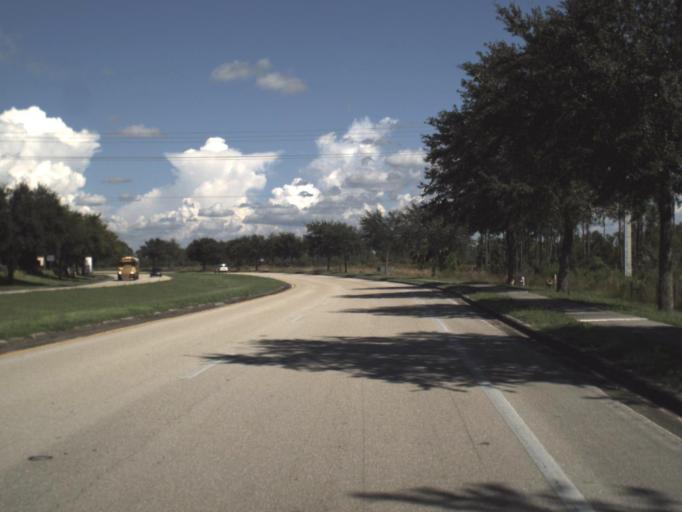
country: US
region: Florida
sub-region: Lee County
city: Palmona Park
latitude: 26.7150
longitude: -81.9255
